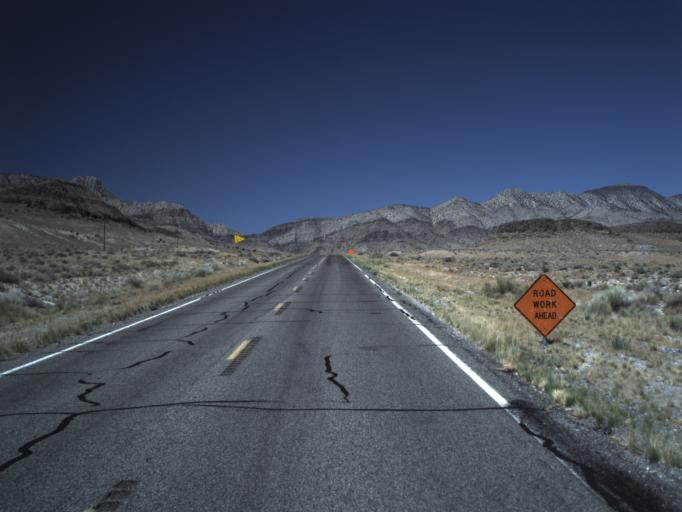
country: US
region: Utah
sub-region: Beaver County
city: Milford
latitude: 39.0842
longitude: -113.5052
